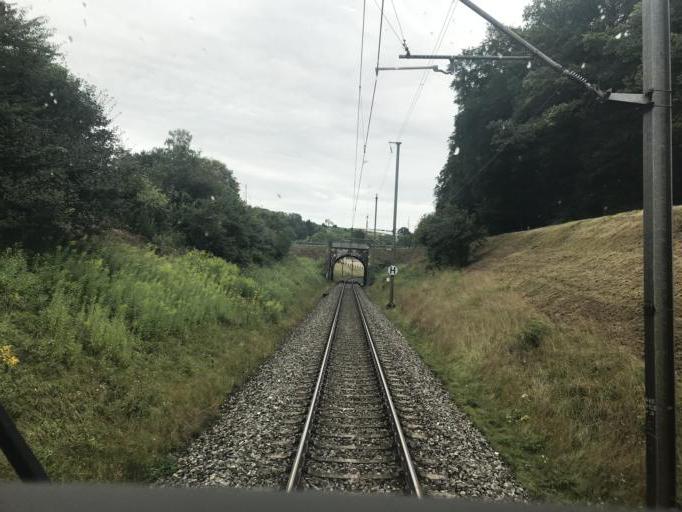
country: DE
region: Baden-Wuerttemberg
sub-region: Freiburg Region
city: Lottstetten
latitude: 47.6208
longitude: 8.5615
